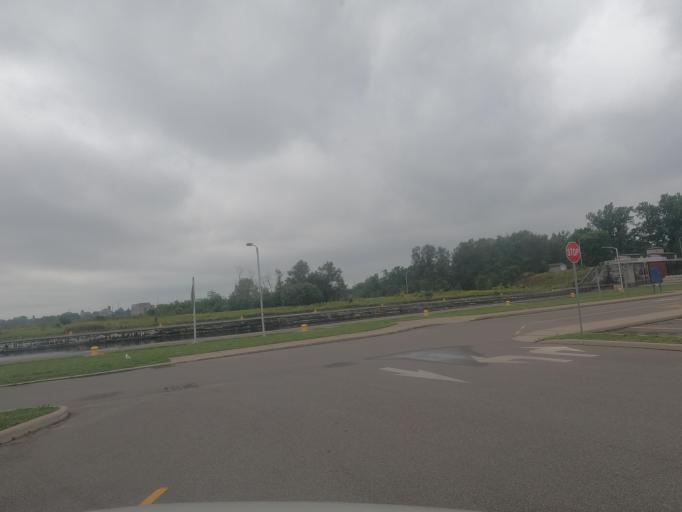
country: CA
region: Ontario
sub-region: Algoma
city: Sault Ste. Marie
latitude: 46.5134
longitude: -84.3480
